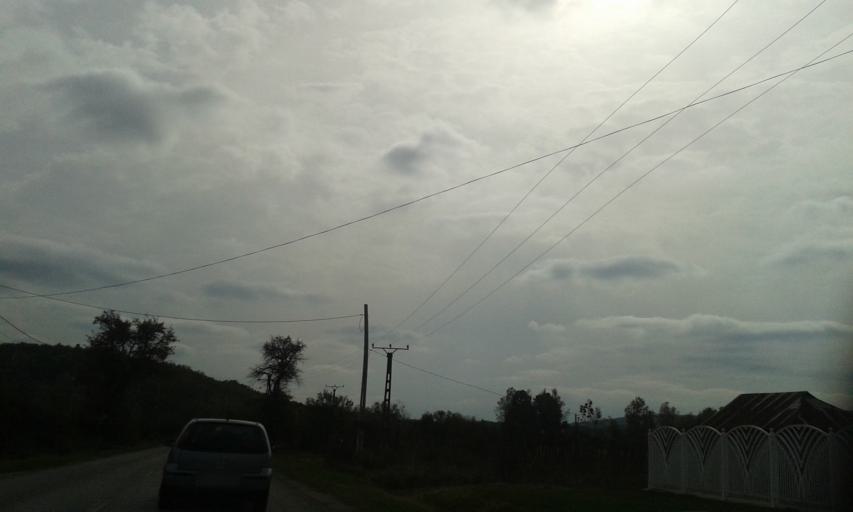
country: RO
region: Gorj
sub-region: Comuna Targu Carbunesti
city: Pojogeni
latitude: 44.9780
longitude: 23.5015
